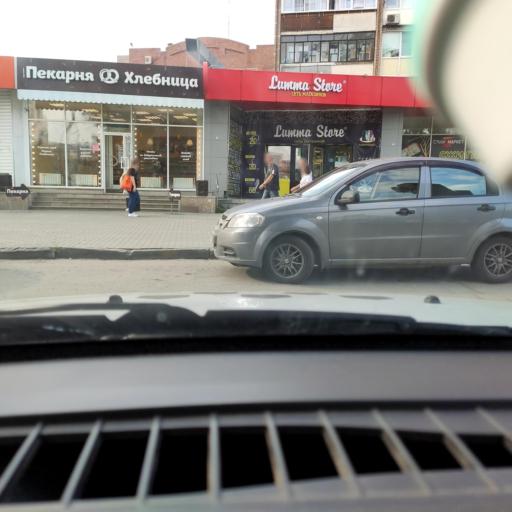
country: RU
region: Sverdlovsk
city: Yekaterinburg
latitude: 56.8567
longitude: 60.6035
